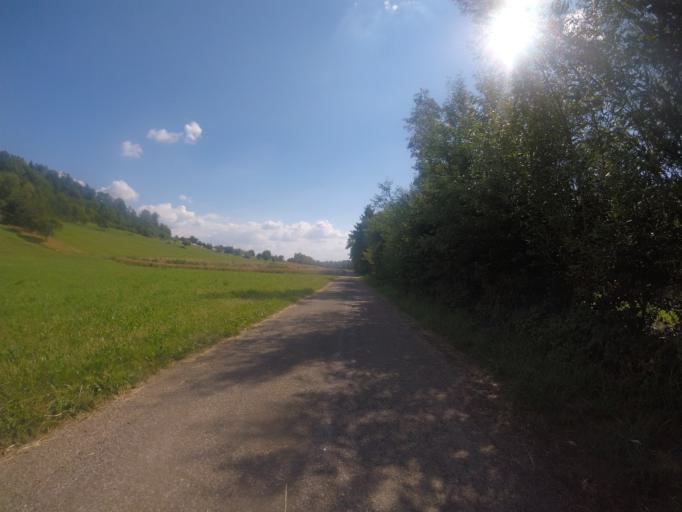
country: DE
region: Baden-Wuerttemberg
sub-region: Regierungsbezirk Stuttgart
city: Beilstein
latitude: 49.0494
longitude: 9.3391
